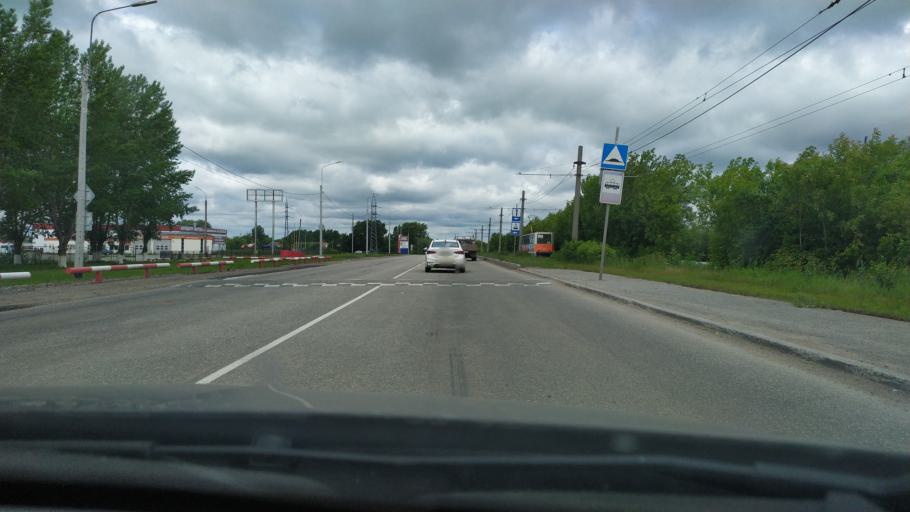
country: RU
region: Perm
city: Kondratovo
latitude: 57.9296
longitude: 56.1301
